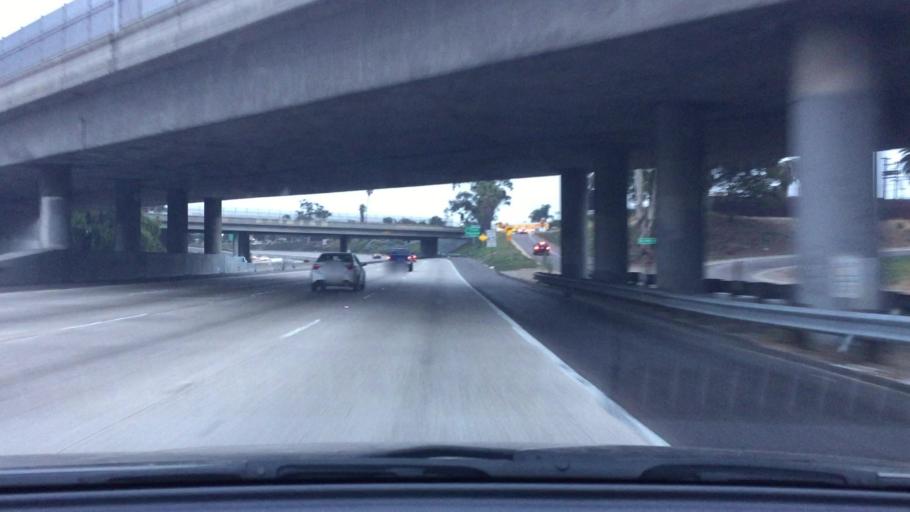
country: US
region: California
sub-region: San Diego County
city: San Diego
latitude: 32.6961
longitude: -117.1357
